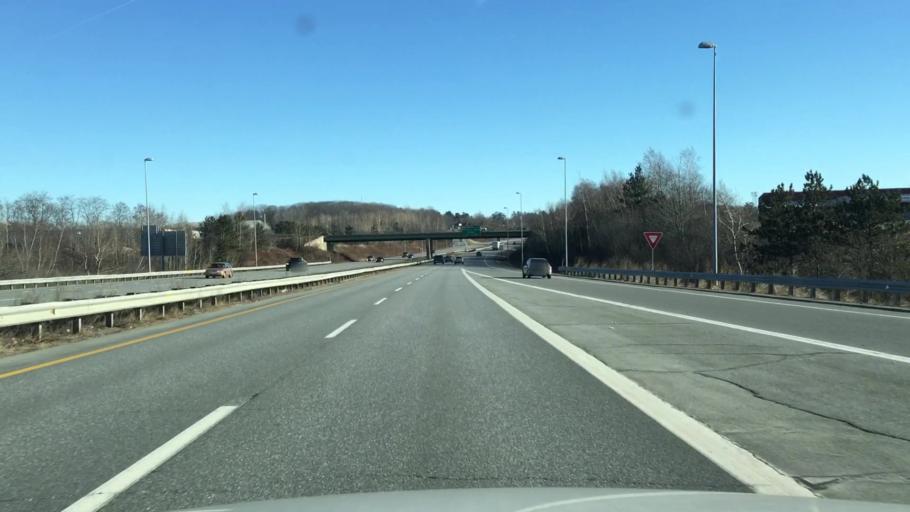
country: US
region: Maine
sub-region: Penobscot County
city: Brewer
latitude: 44.7831
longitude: -68.7683
